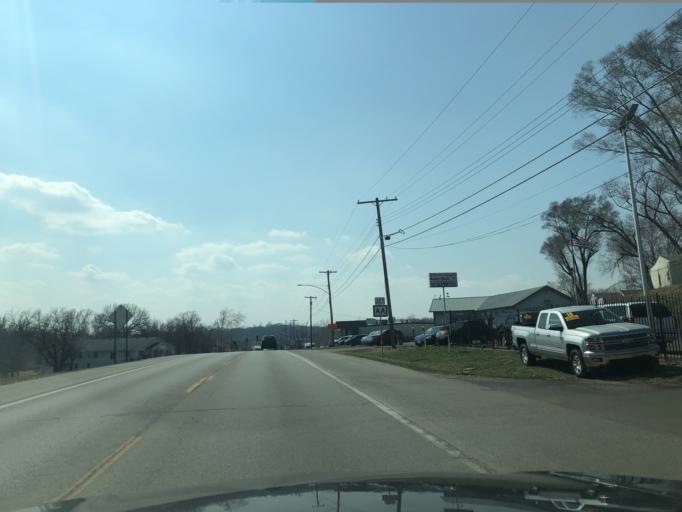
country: US
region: Missouri
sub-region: Platte County
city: Riverside
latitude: 39.1813
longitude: -94.6029
